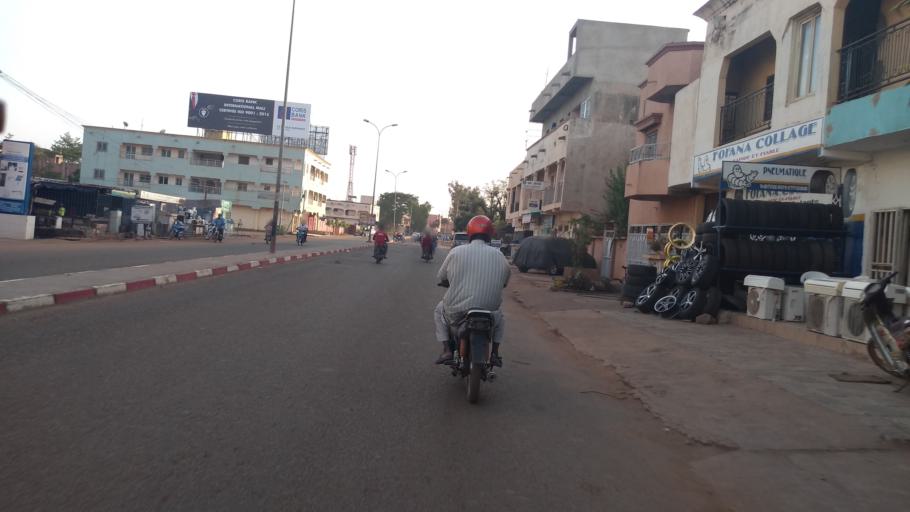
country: ML
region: Bamako
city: Bamako
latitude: 12.6233
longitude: -8.0374
